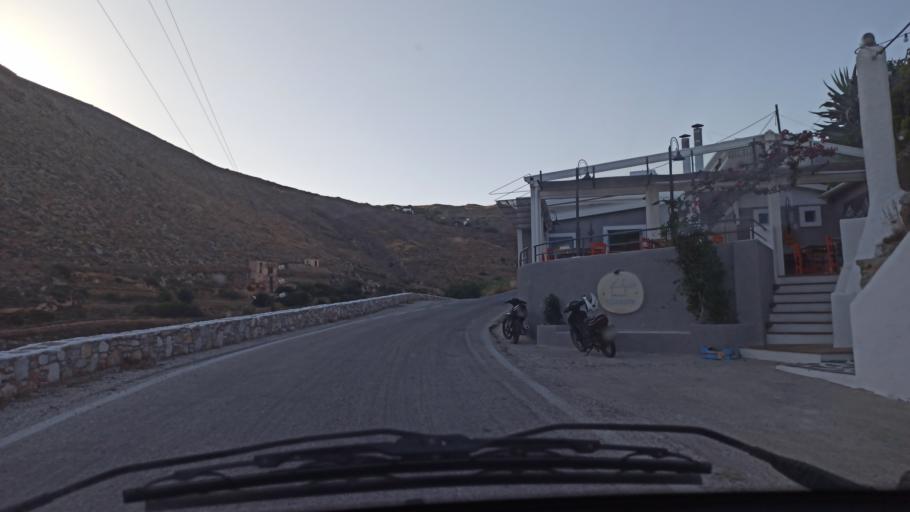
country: GR
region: South Aegean
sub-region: Nomos Kykladon
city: Ano Syros
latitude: 37.4567
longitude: 24.9319
